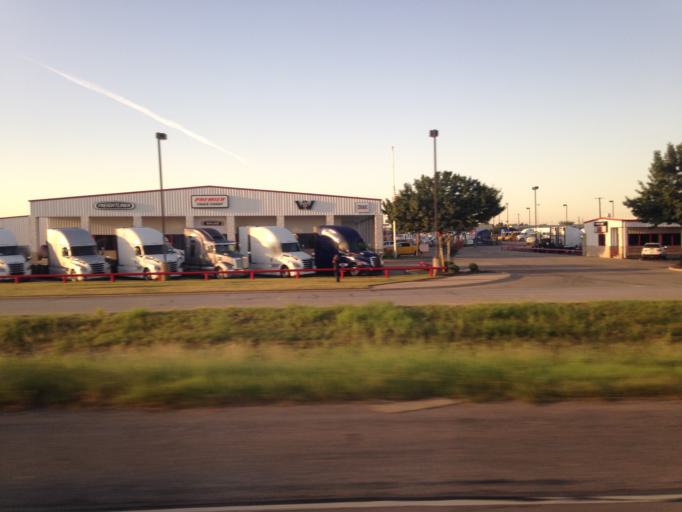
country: US
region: Texas
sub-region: Tarrant County
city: Blue Mound
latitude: 32.8401
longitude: -97.3300
